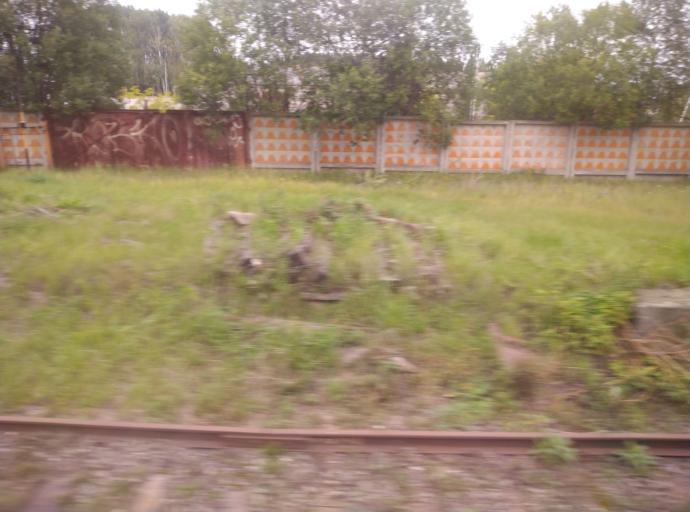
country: RU
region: Kostroma
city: Nerekhta
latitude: 57.4570
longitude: 40.5297
